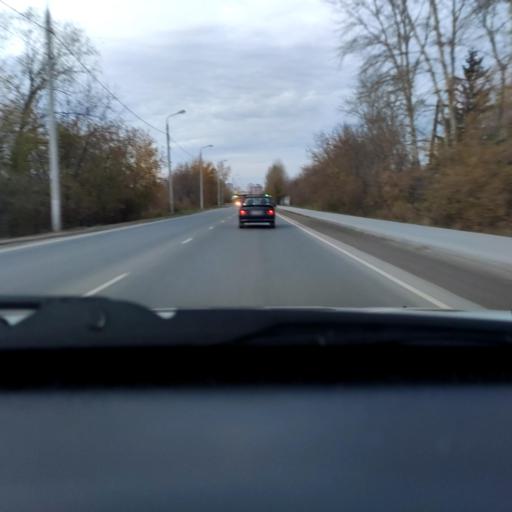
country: RU
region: Perm
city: Kondratovo
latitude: 57.9755
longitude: 56.1292
